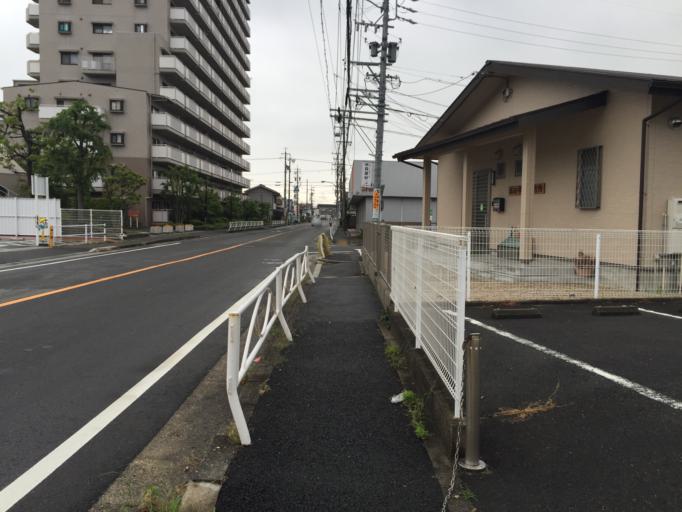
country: JP
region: Mie
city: Yokkaichi
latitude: 34.9601
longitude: 136.6234
